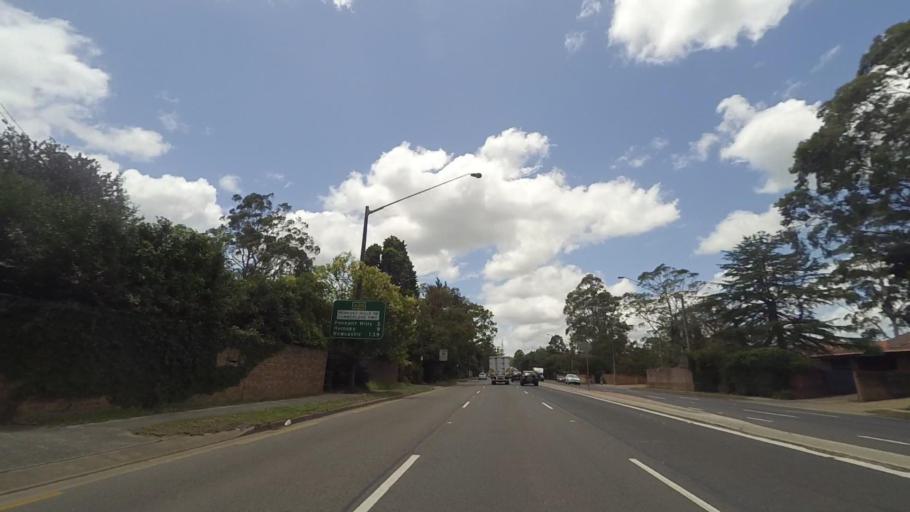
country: AU
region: New South Wales
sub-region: The Hills Shire
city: West Pennant
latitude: -33.7451
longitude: 151.0528
